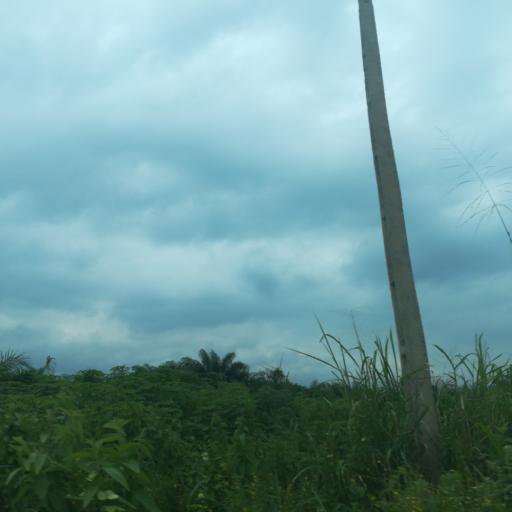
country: NG
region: Lagos
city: Ejirin
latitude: 6.6493
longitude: 3.8297
